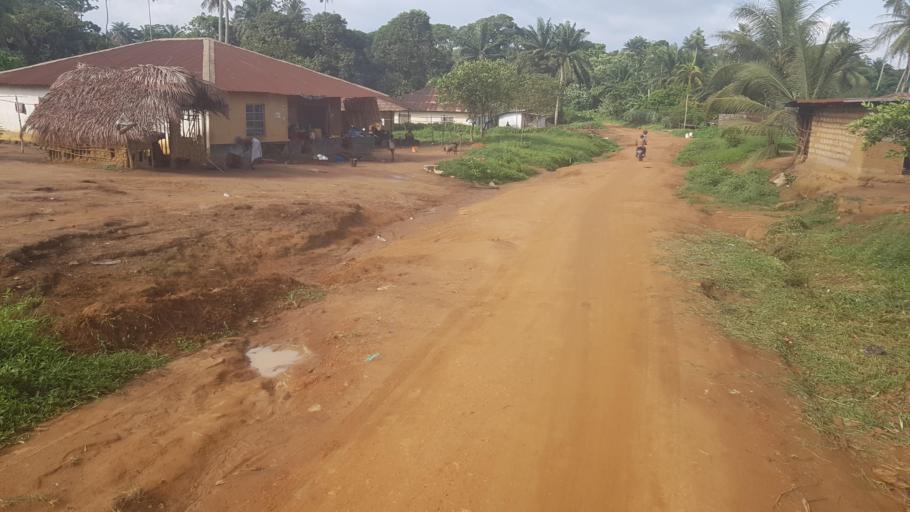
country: SL
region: Southern Province
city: Sumbuya
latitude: 7.6153
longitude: -12.1419
